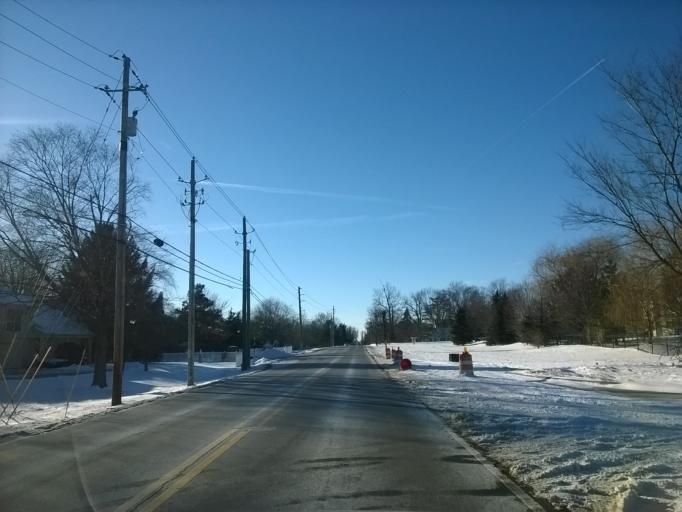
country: US
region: Indiana
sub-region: Boone County
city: Zionsville
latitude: 39.9266
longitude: -86.2076
